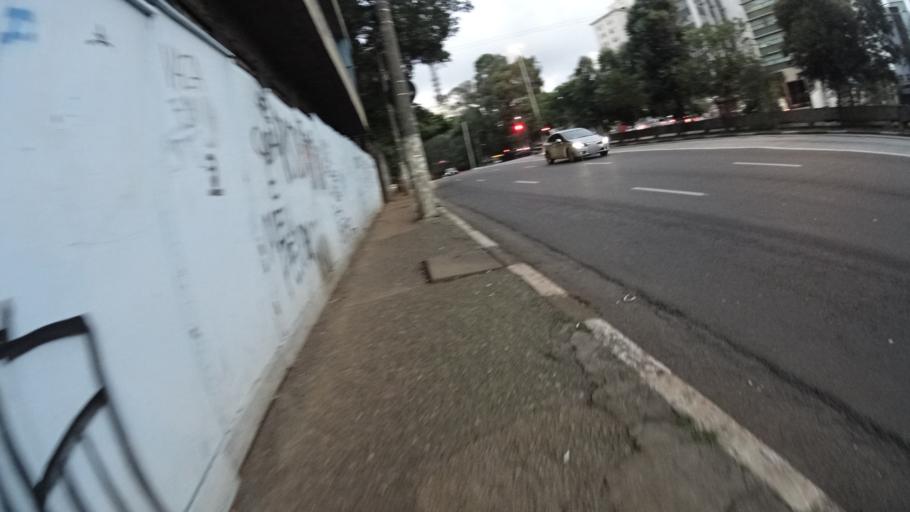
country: BR
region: Sao Paulo
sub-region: Sao Paulo
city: Sao Paulo
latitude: -23.5573
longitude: -46.6669
